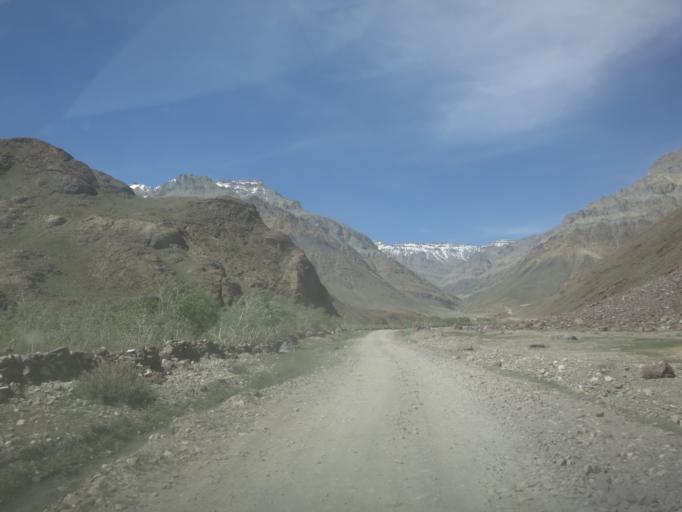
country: IN
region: Himachal Pradesh
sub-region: Kulu
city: Manali
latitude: 32.4416
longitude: 77.6861
